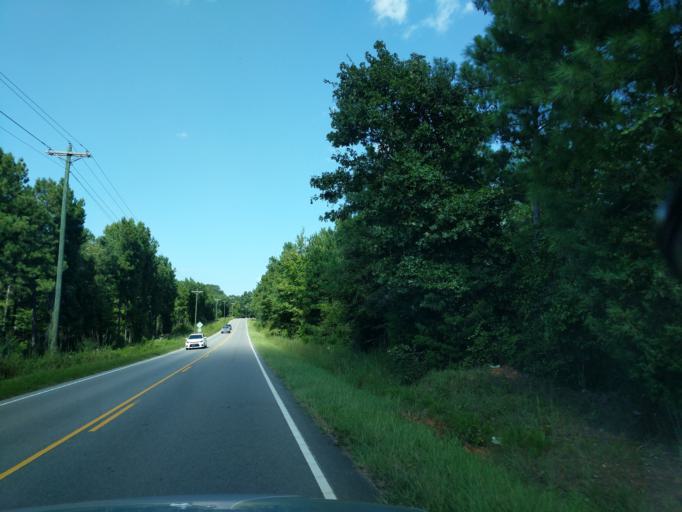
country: US
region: South Carolina
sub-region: Newberry County
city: Prosperity
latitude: 34.1179
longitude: -81.5564
